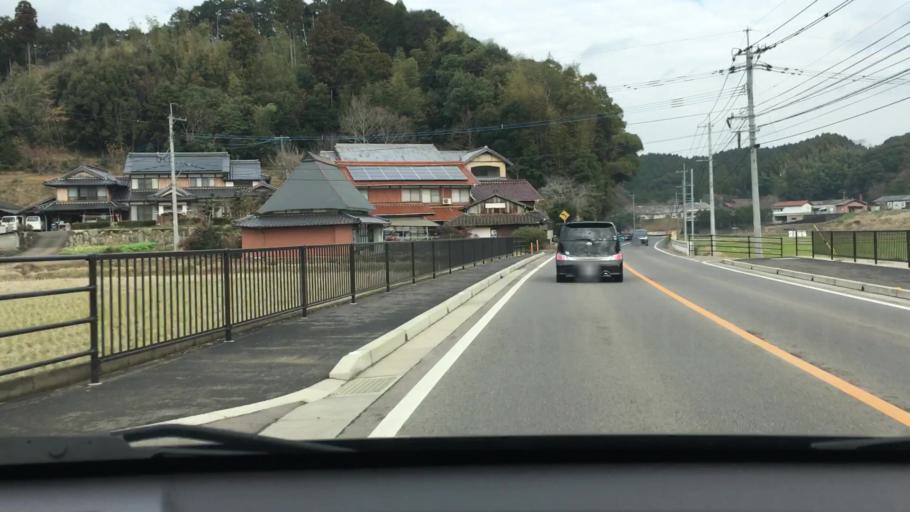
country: JP
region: Saga Prefecture
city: Imaricho-ko
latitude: 33.2965
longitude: 129.9154
